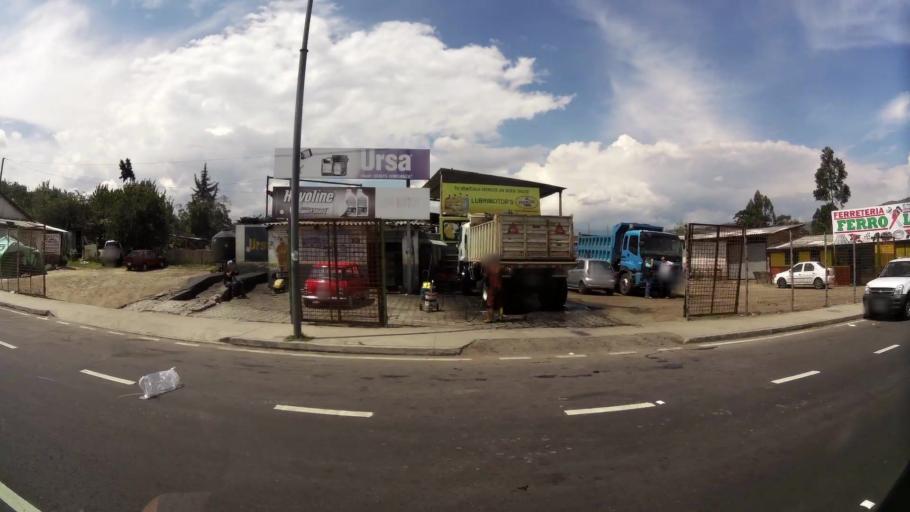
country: EC
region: Pichincha
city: Sangolqui
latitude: -0.2114
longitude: -78.3869
